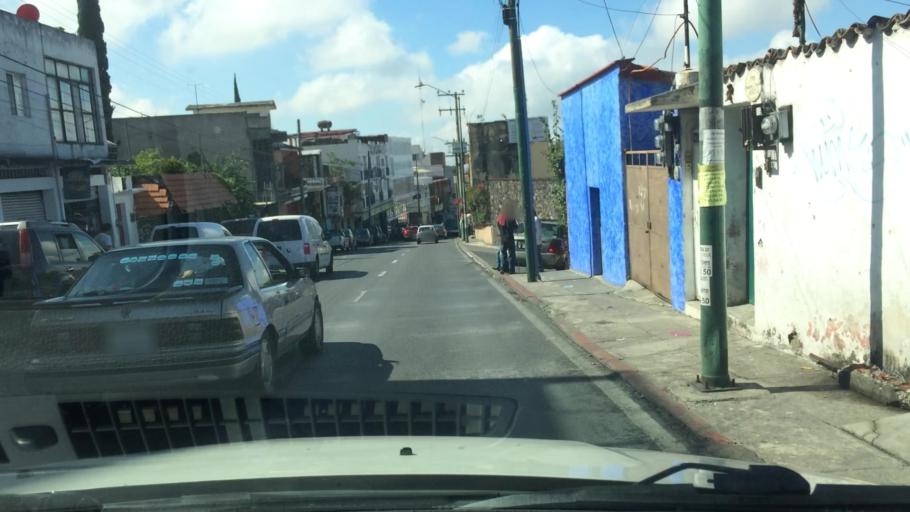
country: MX
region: Morelos
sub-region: Cuernavaca
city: Cuernavaca
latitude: 18.9380
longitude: -99.2410
